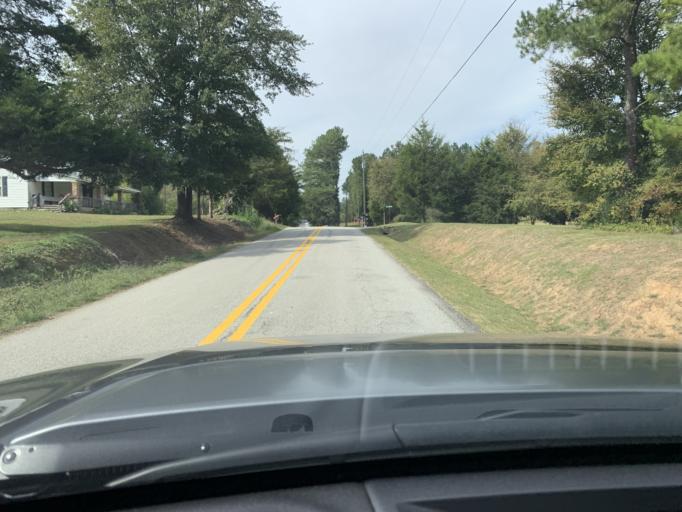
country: US
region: Georgia
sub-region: Polk County
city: Cedartown
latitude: 33.9743
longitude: -85.2787
